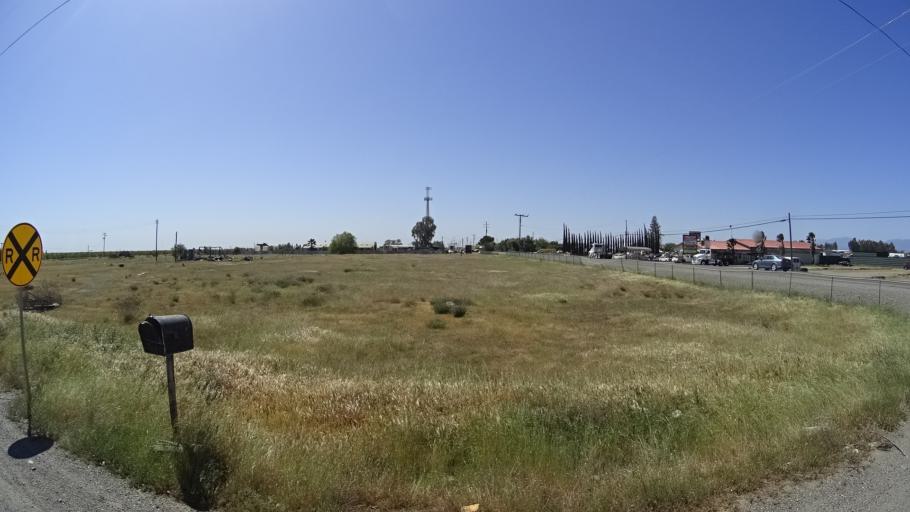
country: US
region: California
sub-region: Glenn County
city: Orland
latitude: 39.6969
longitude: -122.1962
